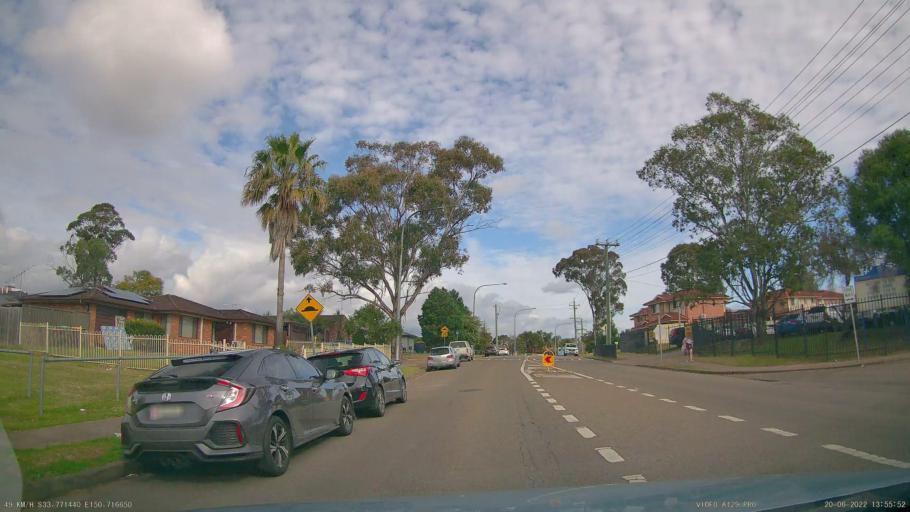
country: AU
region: New South Wales
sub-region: Penrith Municipality
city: Kingswood Park
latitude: -33.7716
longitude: 150.7165
